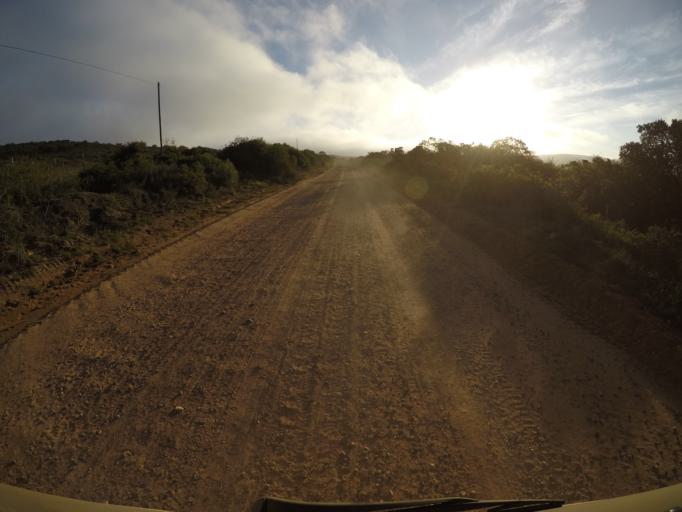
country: ZA
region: Western Cape
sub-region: Eden District Municipality
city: Mossel Bay
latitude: -34.1437
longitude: 22.0231
